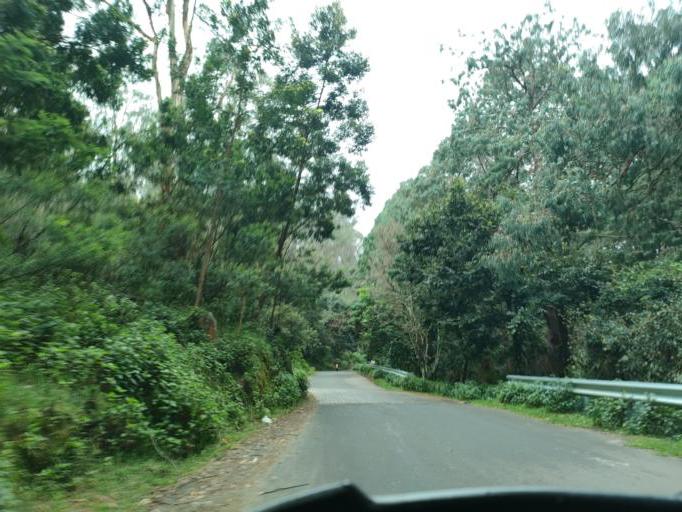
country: IN
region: Tamil Nadu
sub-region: Dindigul
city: Kodaikanal
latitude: 10.2477
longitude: 77.3902
